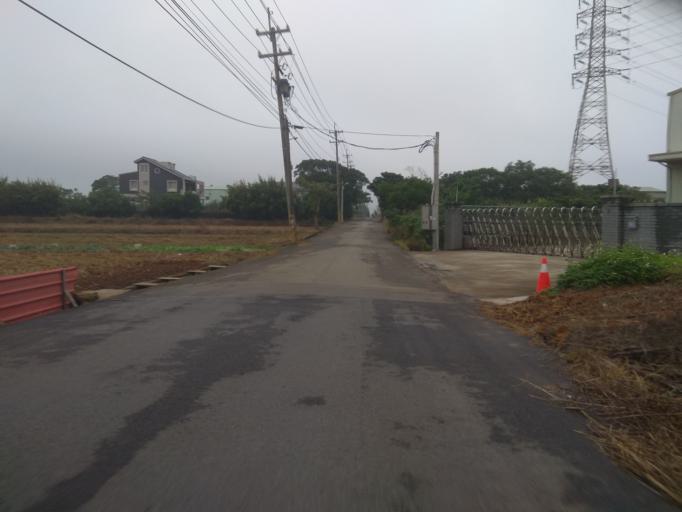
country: TW
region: Taiwan
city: Taoyuan City
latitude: 24.9925
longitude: 121.1256
